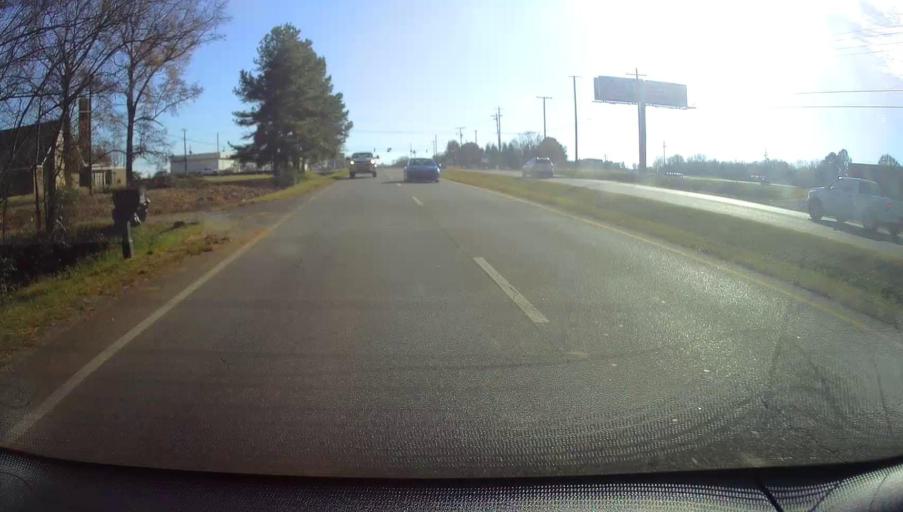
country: US
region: Alabama
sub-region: Limestone County
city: Athens
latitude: 34.7327
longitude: -86.9570
